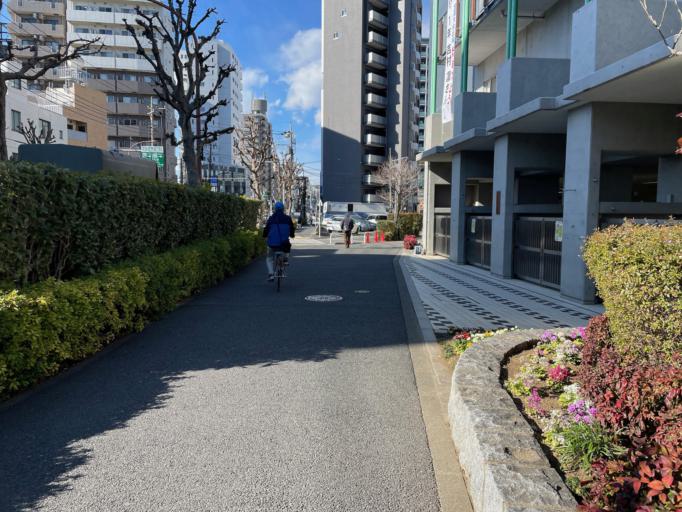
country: JP
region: Tokyo
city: Tokyo
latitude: 35.6149
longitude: 139.7099
